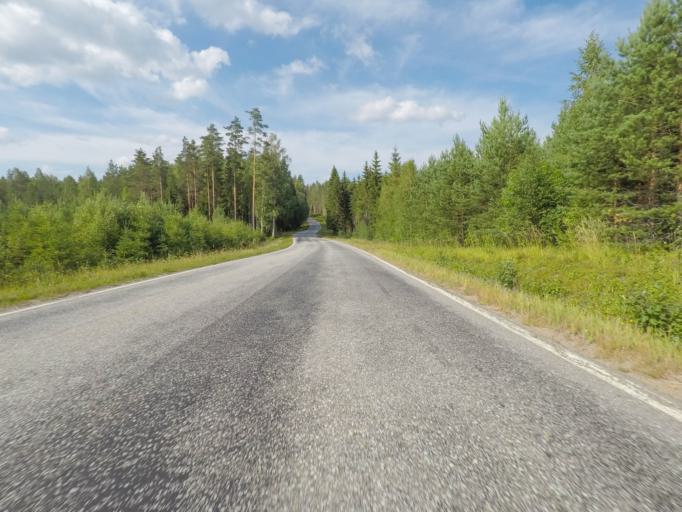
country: FI
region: Southern Savonia
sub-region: Mikkeli
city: Puumala
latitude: 61.6934
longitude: 28.2157
